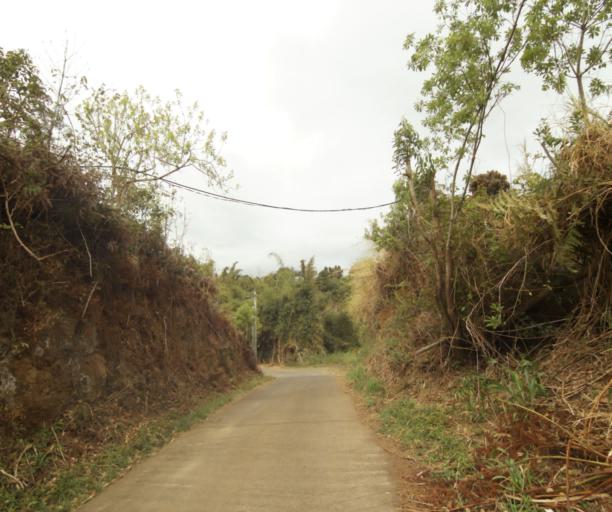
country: RE
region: Reunion
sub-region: Reunion
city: Saint-Paul
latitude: -21.0168
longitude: 55.3302
